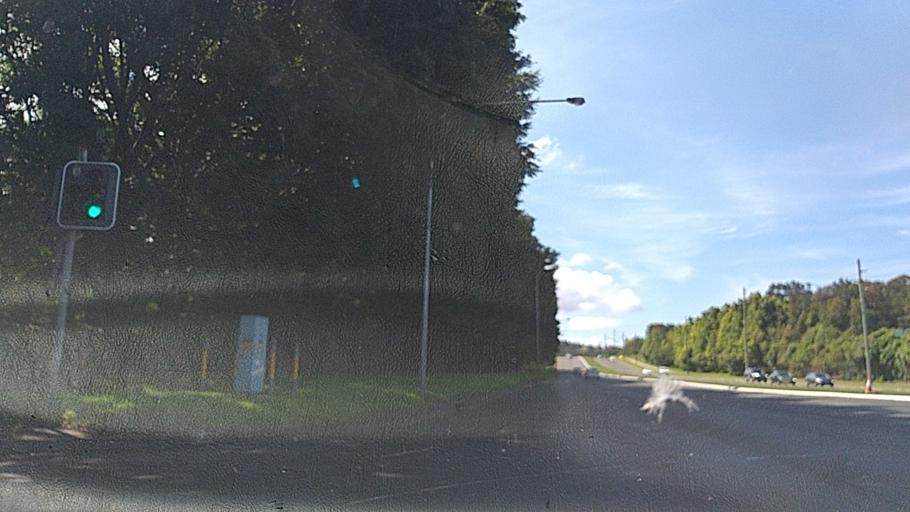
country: AU
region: New South Wales
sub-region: Wollongong
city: Coniston
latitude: -34.4547
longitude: 150.8734
